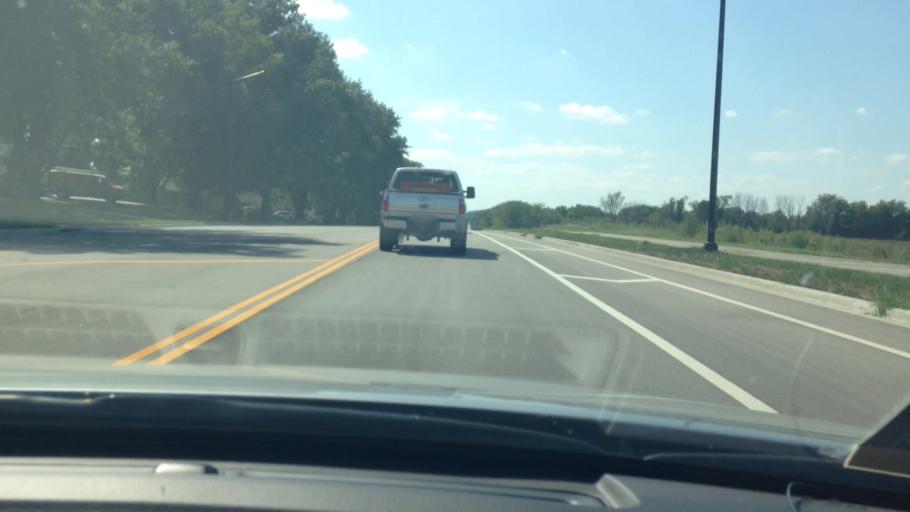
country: US
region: Kansas
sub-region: Johnson County
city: Lenexa
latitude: 38.8692
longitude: -94.7249
